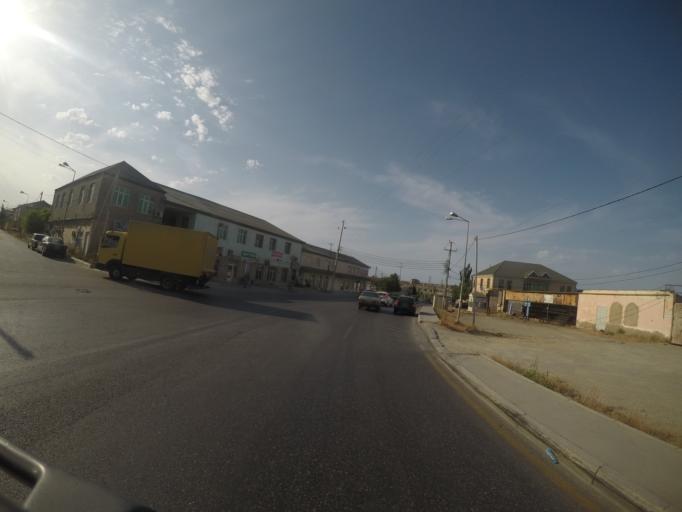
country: AZ
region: Baki
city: Binagadi
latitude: 40.4763
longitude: 49.8332
